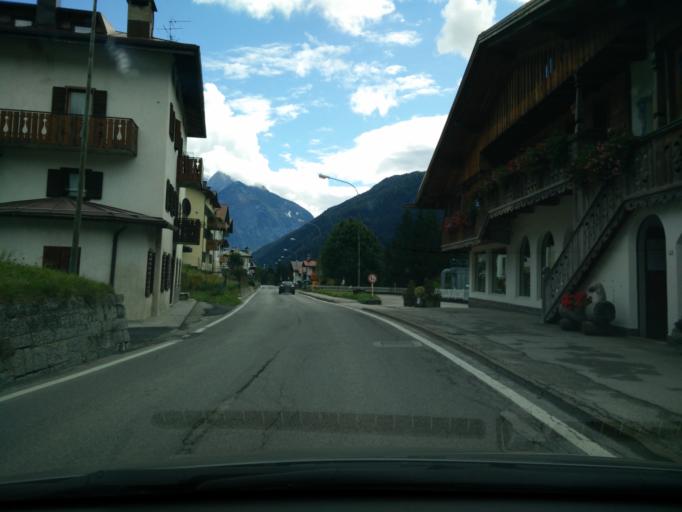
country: IT
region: Veneto
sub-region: Provincia di Belluno
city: Auronzo
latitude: 46.5596
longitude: 12.4216
